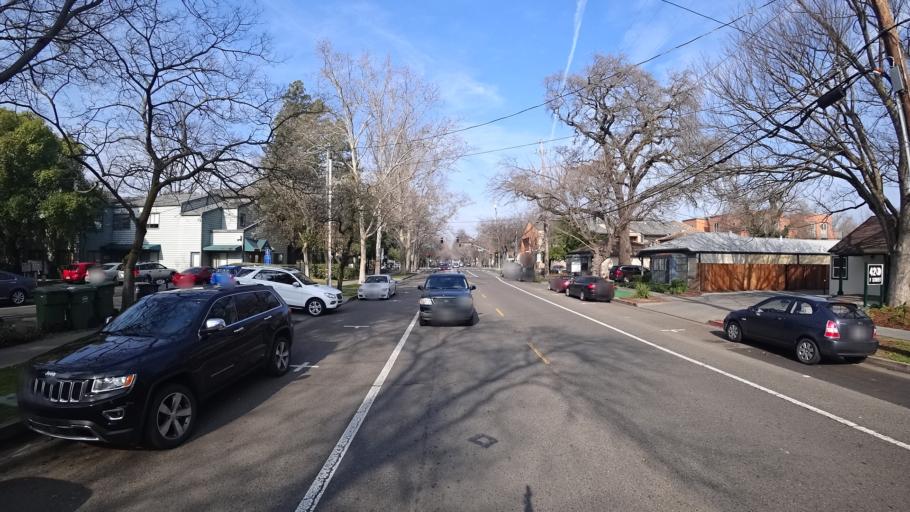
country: US
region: California
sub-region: Yolo County
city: Davis
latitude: 38.5465
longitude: -121.7409
